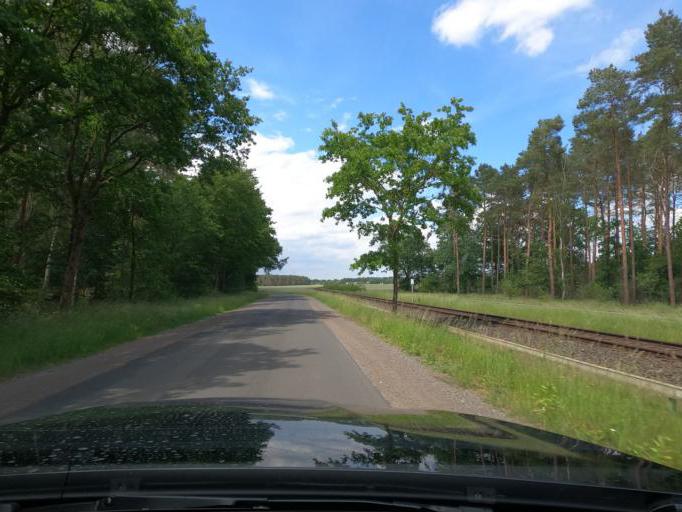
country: DE
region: Lower Saxony
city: Schwarmstedt
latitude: 52.6542
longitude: 9.6258
